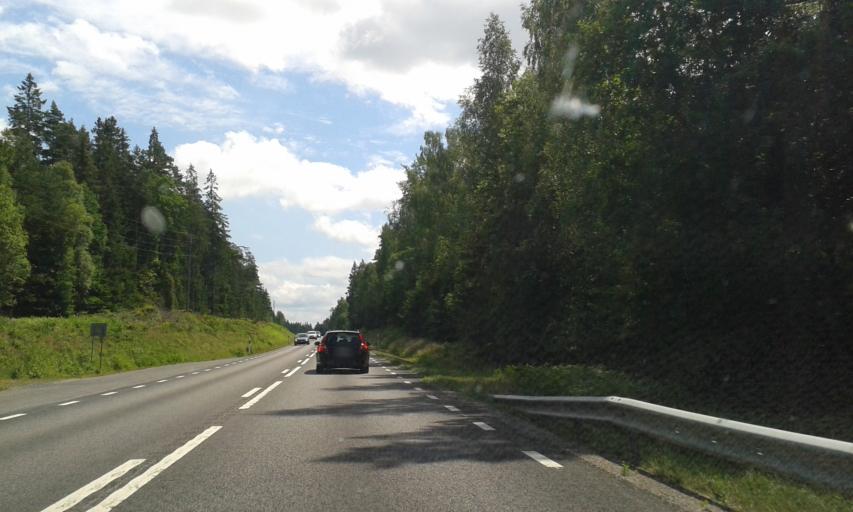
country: SE
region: Joenkoeping
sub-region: Varnamo Kommun
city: Bor
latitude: 57.0578
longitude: 14.2029
